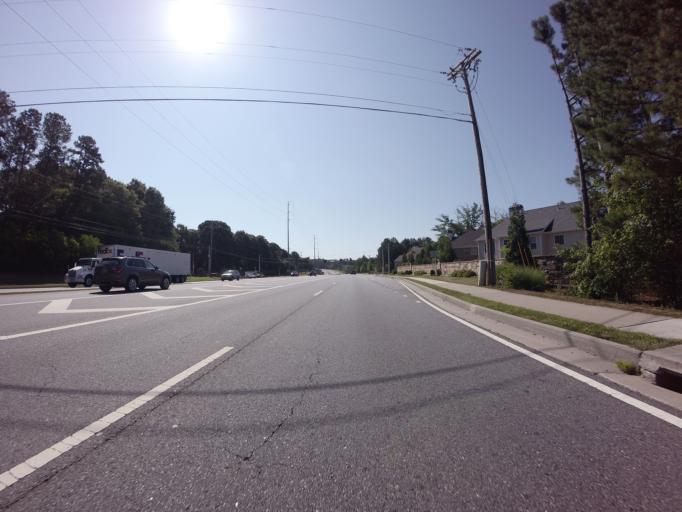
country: US
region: Georgia
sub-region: Gwinnett County
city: Duluth
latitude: 34.0581
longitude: -84.1499
